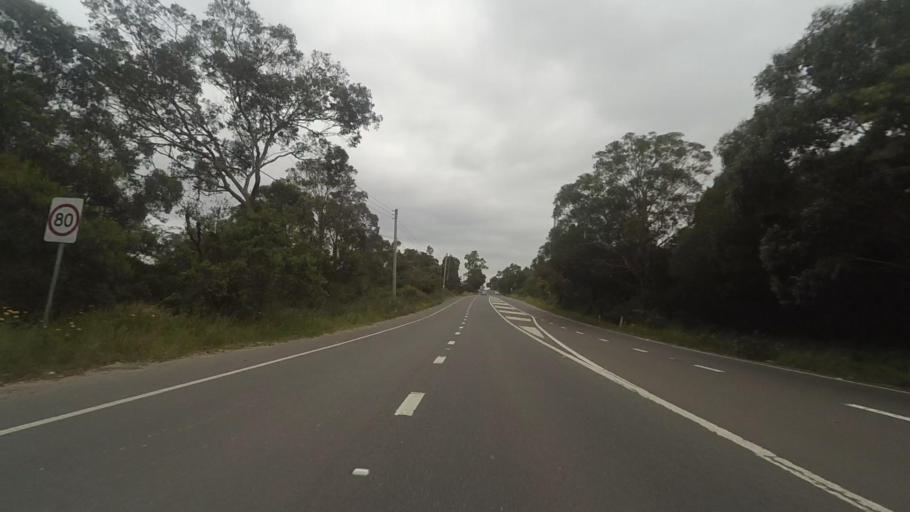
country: AU
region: New South Wales
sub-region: Sutherland Shire
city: Engadine
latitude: -34.0407
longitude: 150.9967
